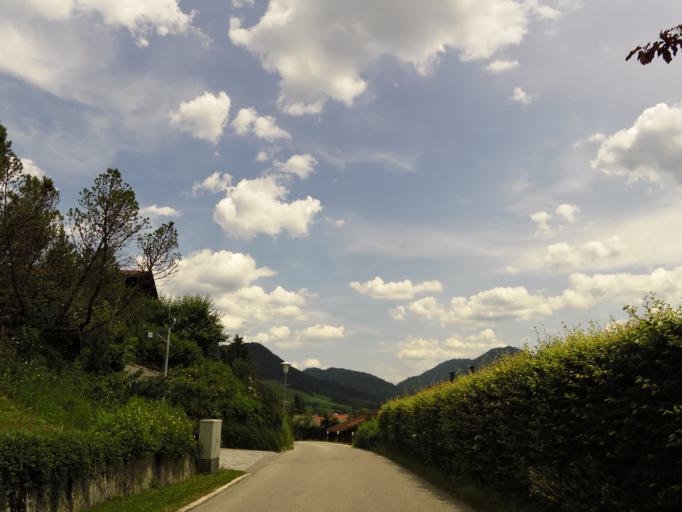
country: DE
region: Bavaria
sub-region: Upper Bavaria
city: Reit im Winkl
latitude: 47.6745
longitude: 12.4607
